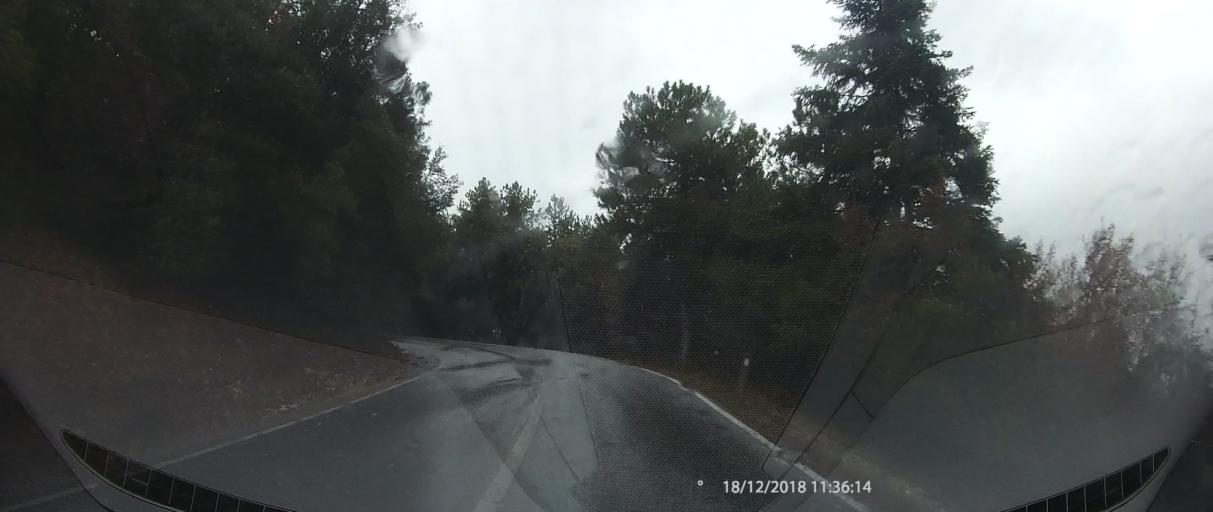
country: GR
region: Central Macedonia
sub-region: Nomos Pierias
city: Litochoro
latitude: 40.1158
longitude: 22.4828
